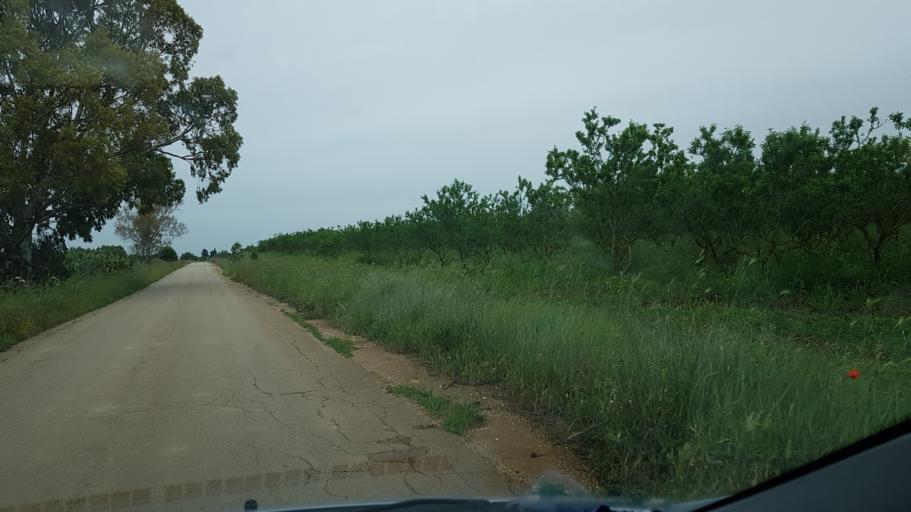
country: IT
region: Apulia
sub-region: Provincia di Brindisi
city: Mesagne
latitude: 40.6202
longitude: 17.7771
